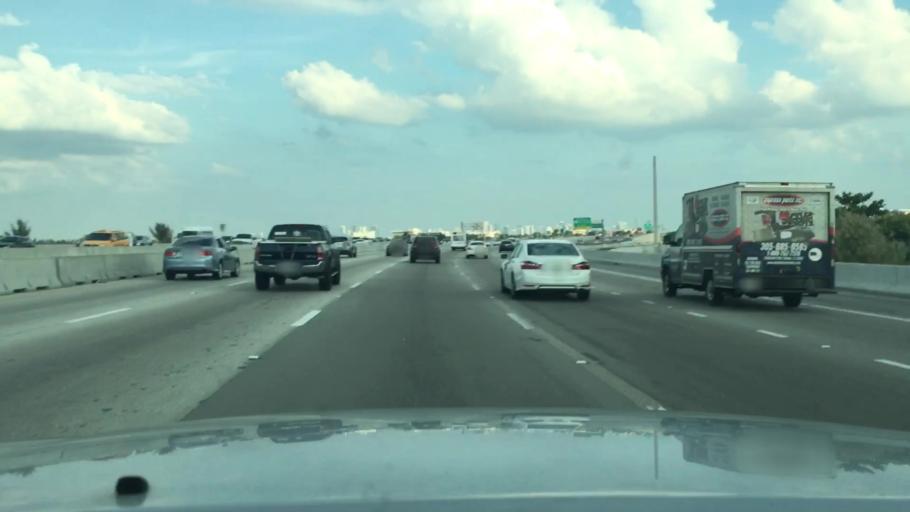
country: US
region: Florida
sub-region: Miami-Dade County
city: West Miami
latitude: 25.7850
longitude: -80.2801
